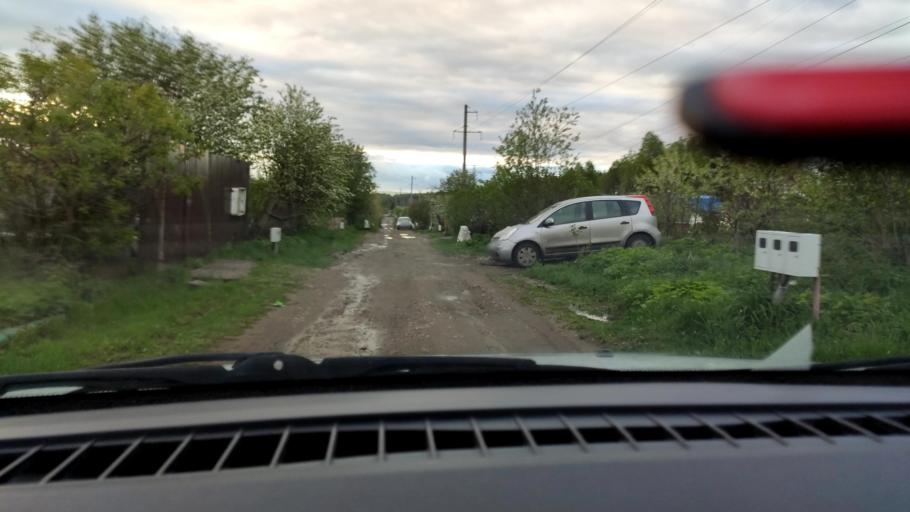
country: RU
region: Perm
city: Polazna
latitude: 58.1288
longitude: 56.4154
